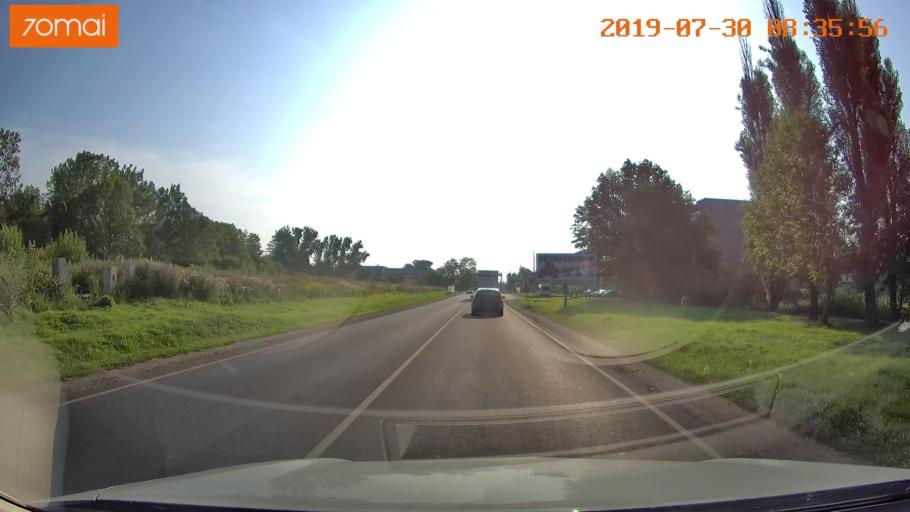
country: RU
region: Kaliningrad
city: Chernyakhovsk
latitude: 54.6346
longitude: 21.7871
